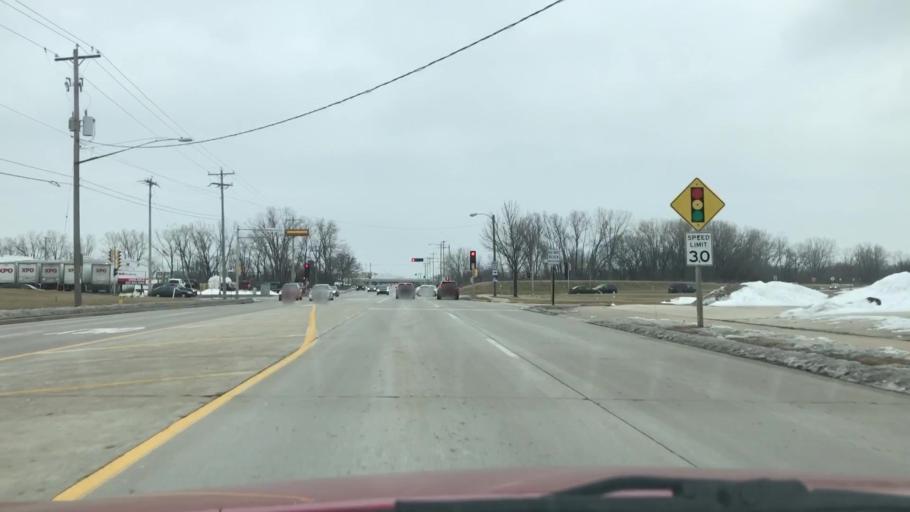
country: US
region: Wisconsin
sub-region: Brown County
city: Ashwaubenon
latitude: 44.4751
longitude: -88.0696
